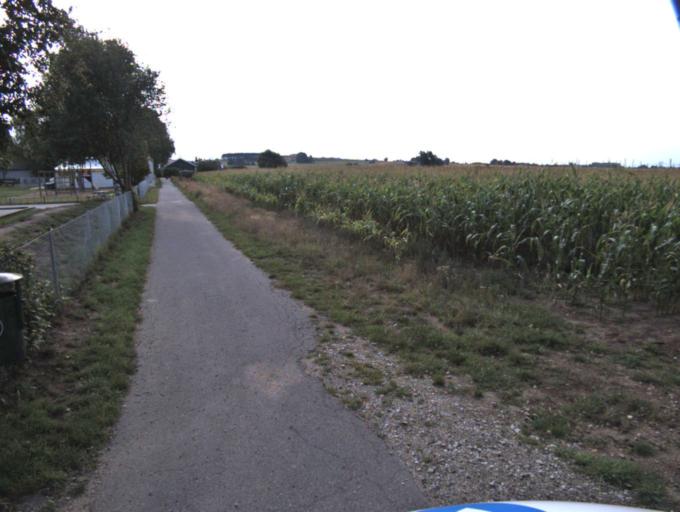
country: SE
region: Skane
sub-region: Kavlinge Kommun
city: Loddekopinge
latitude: 55.8187
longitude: 13.0172
